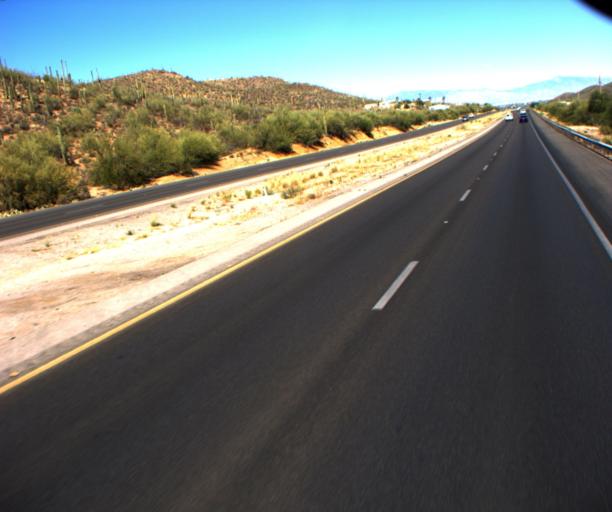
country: US
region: Arizona
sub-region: Pima County
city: Drexel Heights
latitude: 32.1769
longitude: -111.0339
